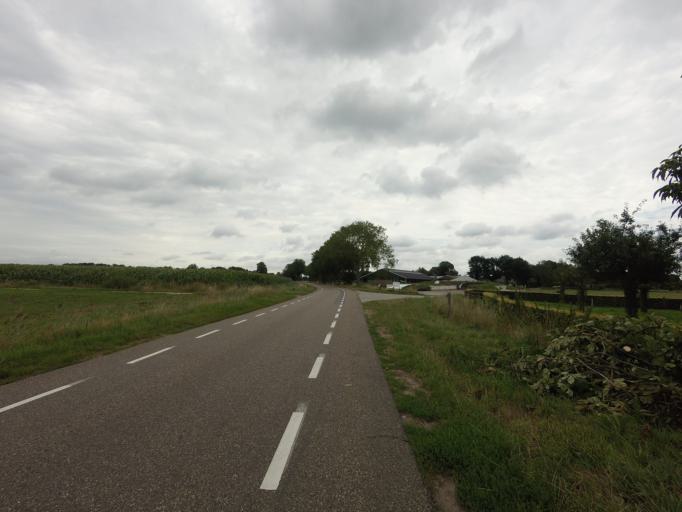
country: NL
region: Gelderland
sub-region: Gemeente Lochem
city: Laren
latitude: 52.2908
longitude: 6.3516
